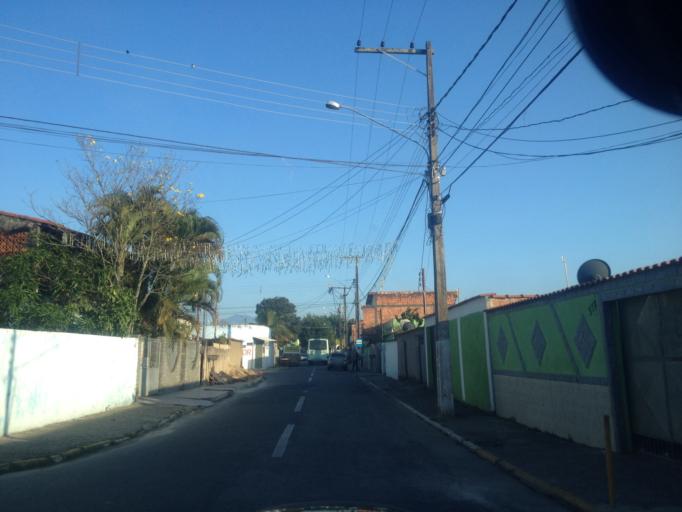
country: BR
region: Rio de Janeiro
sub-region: Porto Real
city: Porto Real
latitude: -22.4145
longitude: -44.3041
